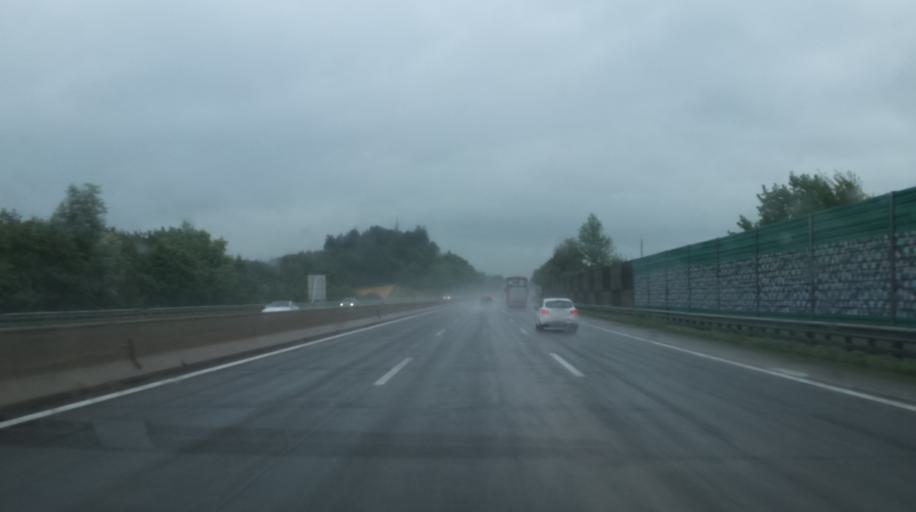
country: AT
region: Lower Austria
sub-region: Politischer Bezirk Amstetten
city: Haag
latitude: 48.1456
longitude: 14.5715
